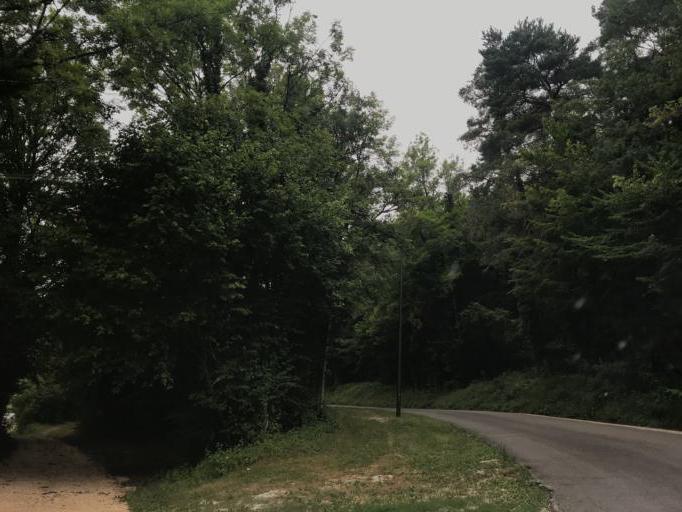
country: FR
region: Rhone-Alpes
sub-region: Departement de l'Ain
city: Dortan
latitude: 46.3440
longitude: 5.6471
